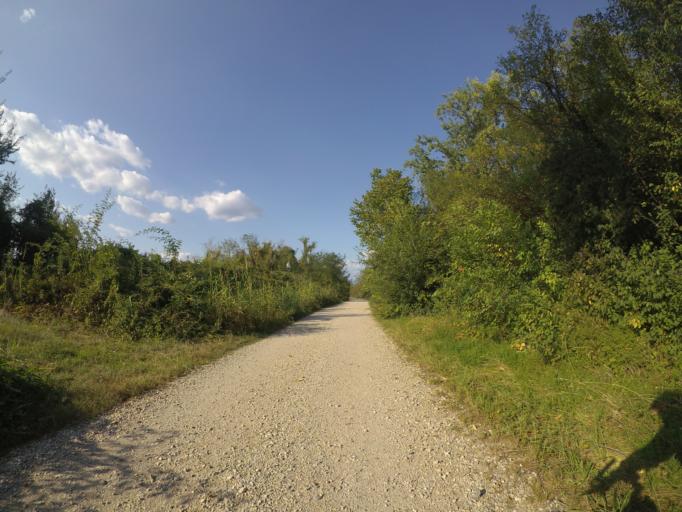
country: IT
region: Friuli Venezia Giulia
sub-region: Provincia di Udine
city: Basaldella
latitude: 46.0231
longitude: 13.1975
